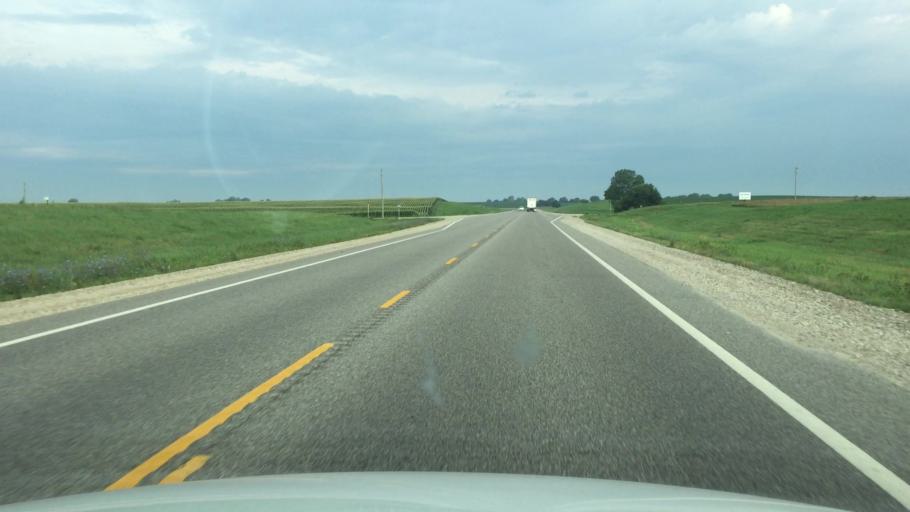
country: US
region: Kansas
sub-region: Doniphan County
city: Highland
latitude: 39.8290
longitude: -95.2259
